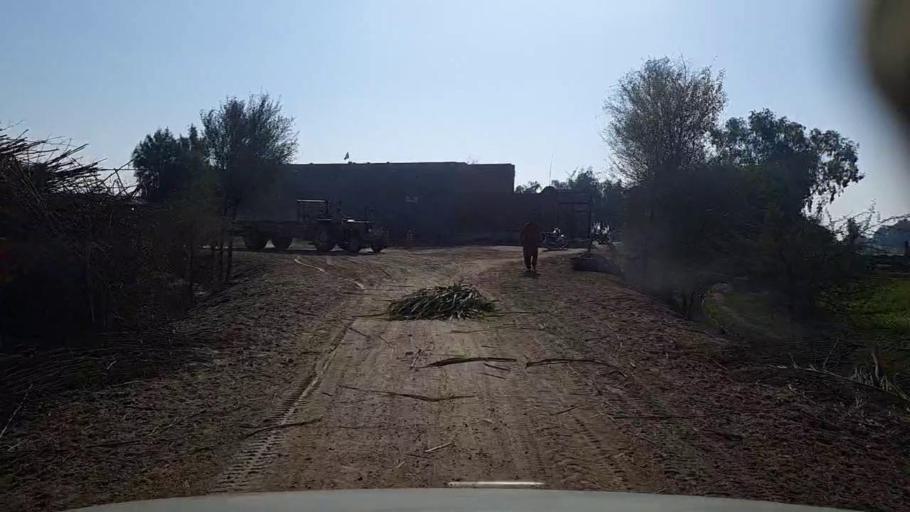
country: PK
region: Sindh
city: Khairpur
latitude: 28.0548
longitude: 69.7387
